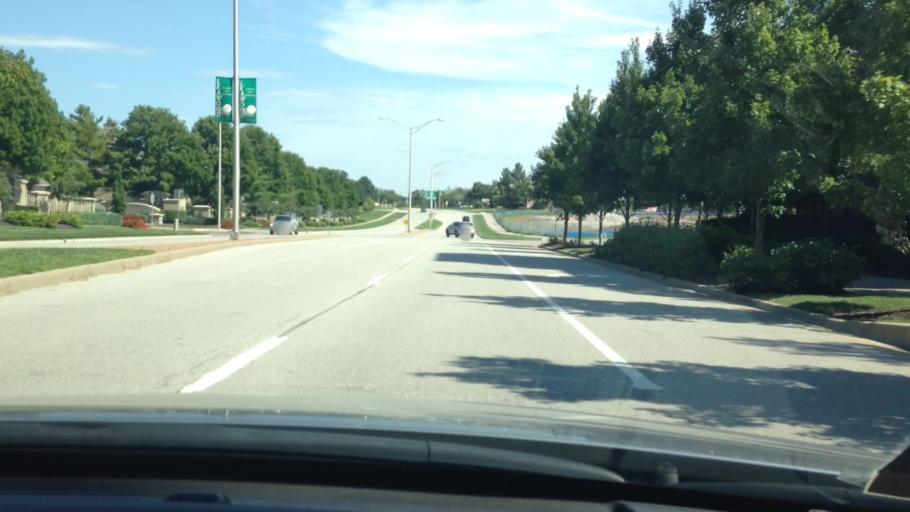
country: US
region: Kansas
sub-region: Johnson County
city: Leawood
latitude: 38.9188
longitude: -94.6458
